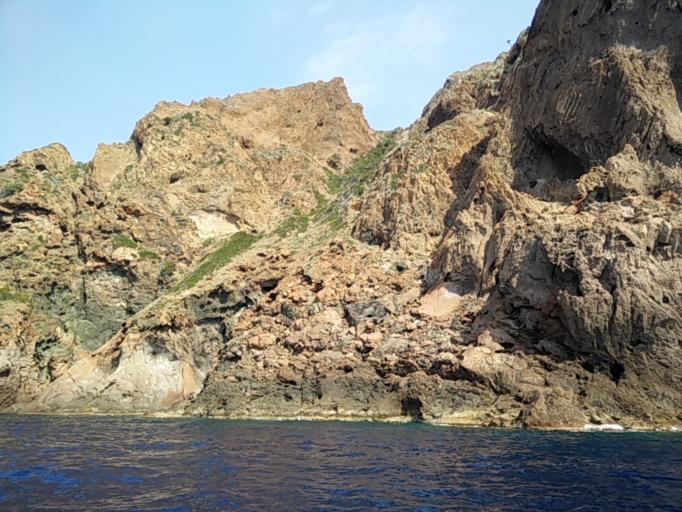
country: FR
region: Corsica
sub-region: Departement de la Corse-du-Sud
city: Cargese
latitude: 42.3481
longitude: 8.5517
